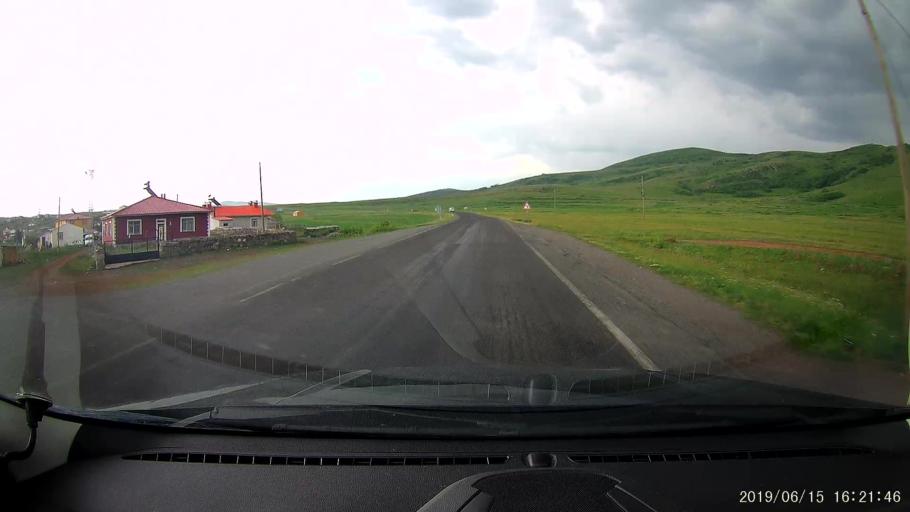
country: TR
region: Ardahan
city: Hanak
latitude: 41.1953
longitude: 42.8456
